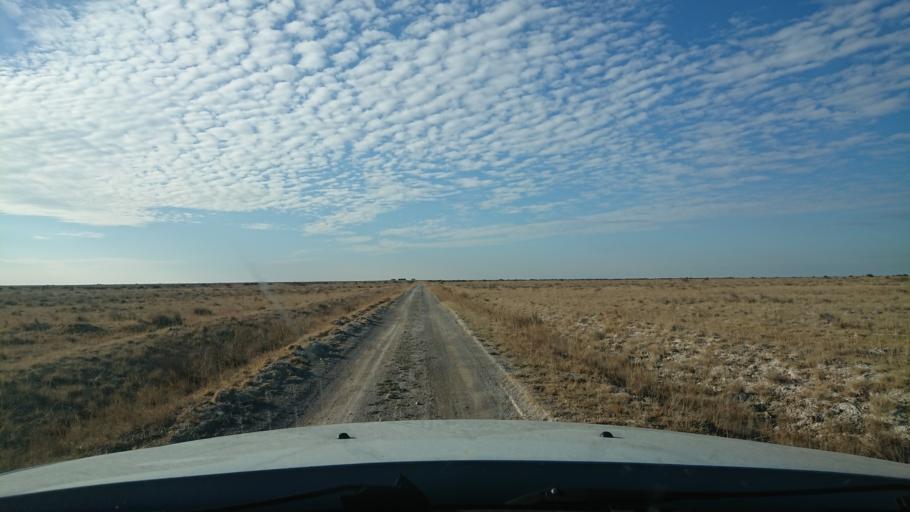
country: TR
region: Aksaray
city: Eskil
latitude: 38.5429
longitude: 33.3304
